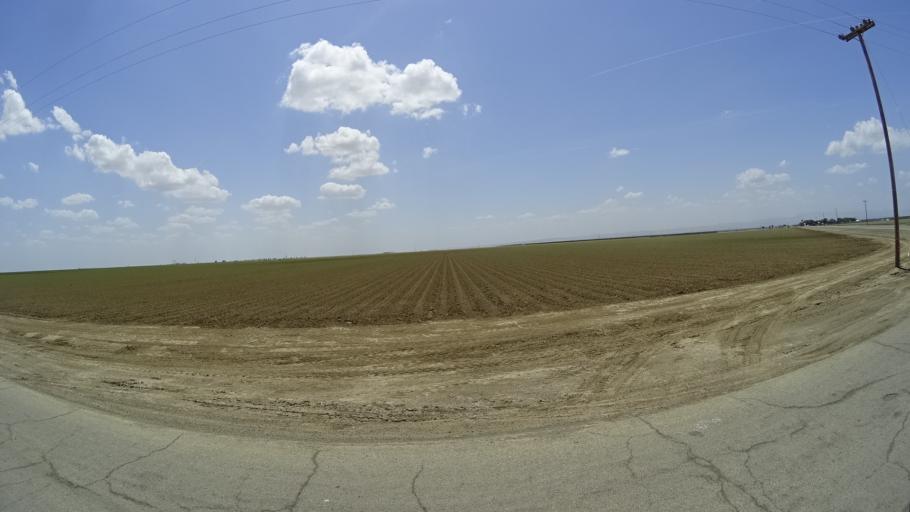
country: US
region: California
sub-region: Kings County
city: Lemoore Station
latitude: 36.1894
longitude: -119.9451
